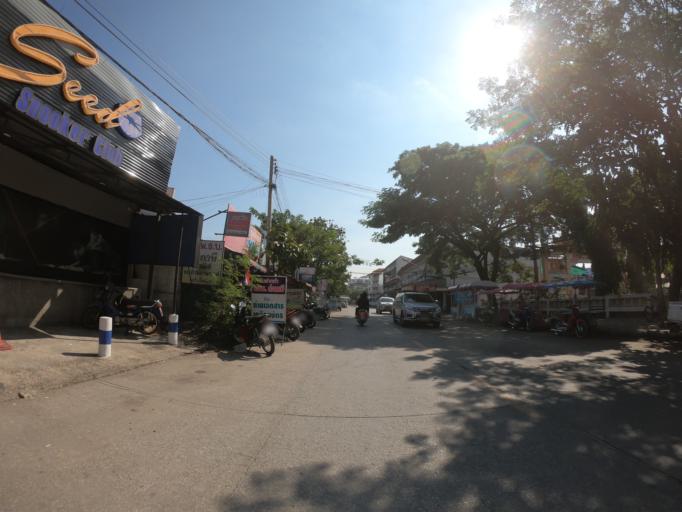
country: TH
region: Chiang Mai
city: Chiang Mai
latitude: 18.7998
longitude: 98.9970
